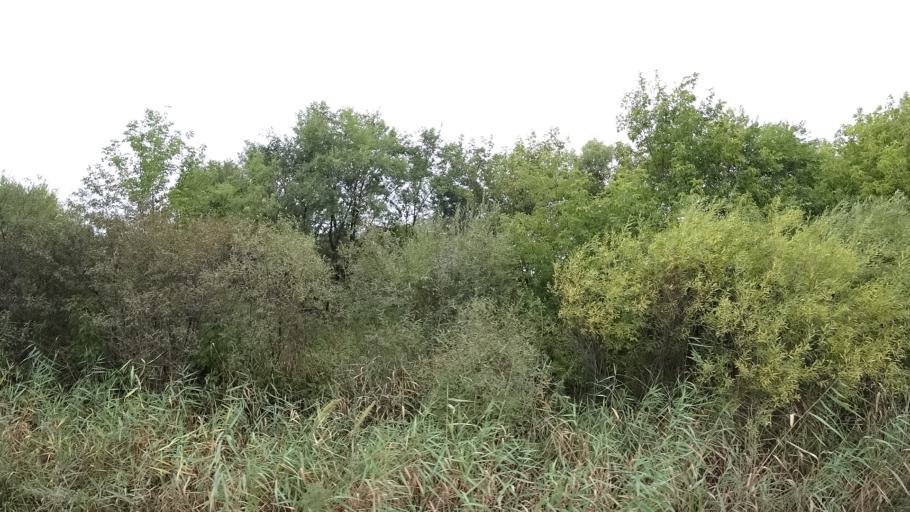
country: RU
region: Primorskiy
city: Monastyrishche
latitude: 44.1883
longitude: 132.4828
